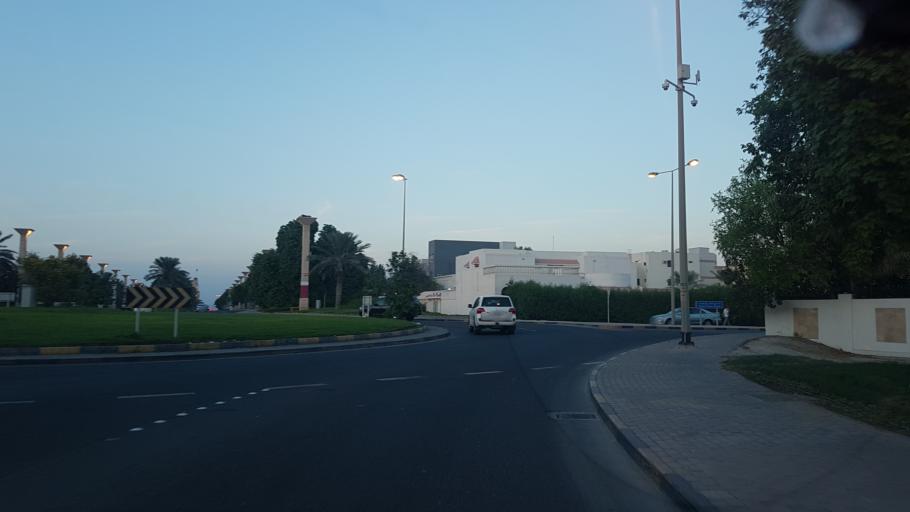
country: BH
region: Northern
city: Ar Rifa'
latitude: 26.1279
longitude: 50.5373
